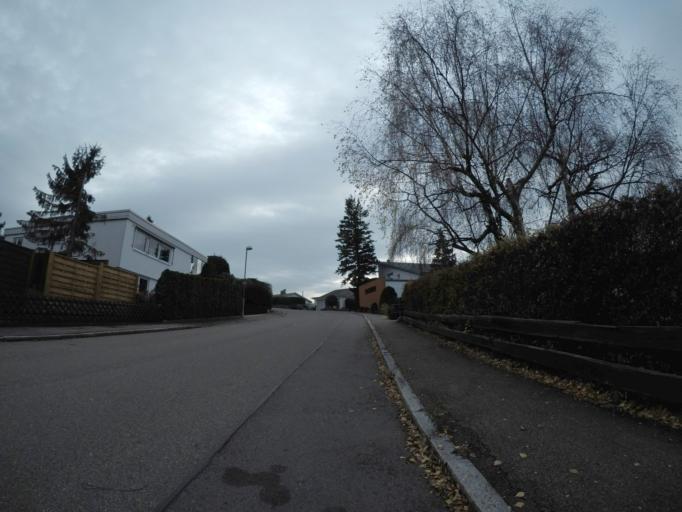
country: DE
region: Baden-Wuerttemberg
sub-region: Tuebingen Region
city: Reutlingen
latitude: 48.5020
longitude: 9.2287
